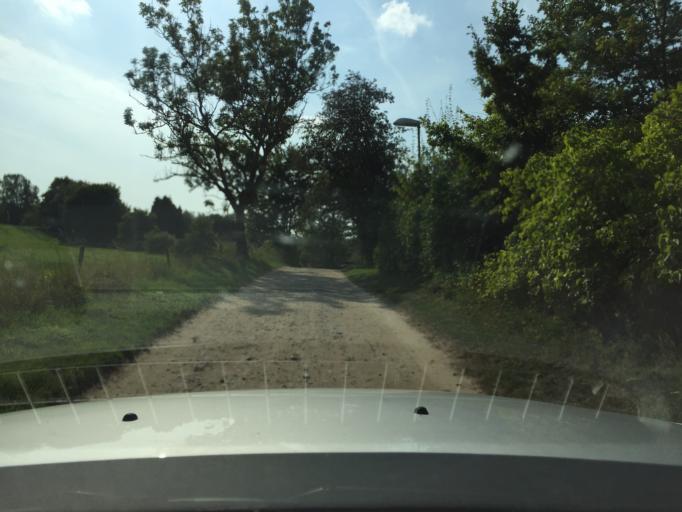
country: SE
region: Skane
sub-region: Kristianstads Kommun
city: Degeberga
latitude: 55.7260
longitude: 14.1119
